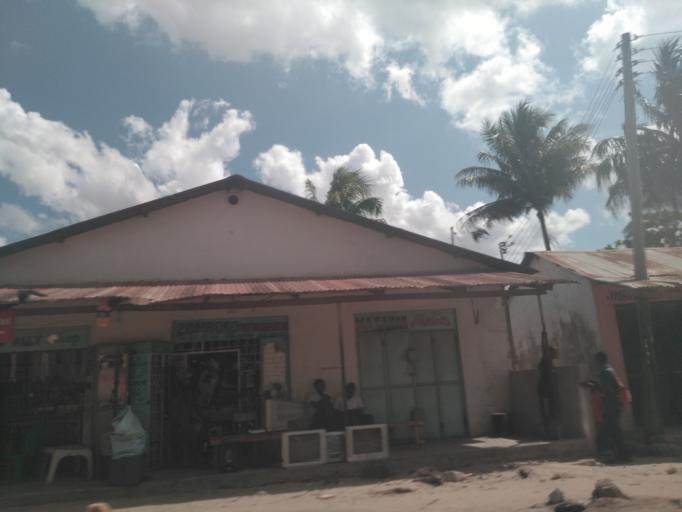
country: TZ
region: Dar es Salaam
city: Dar es Salaam
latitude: -6.8733
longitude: 39.2389
